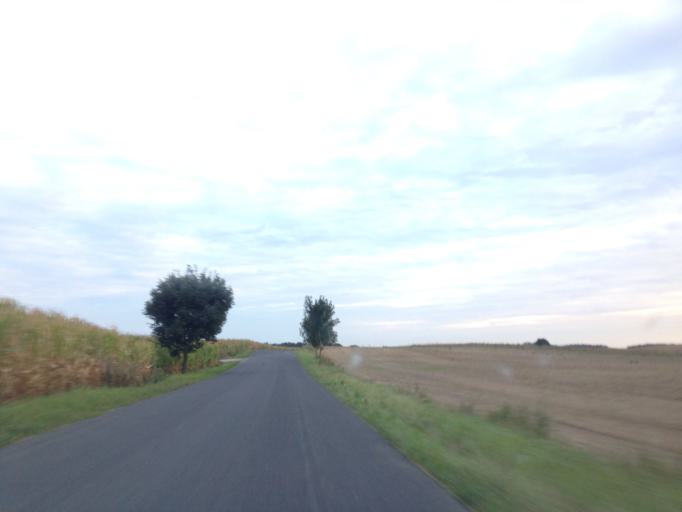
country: PL
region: Kujawsko-Pomorskie
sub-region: Powiat brodnicki
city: Brzozie
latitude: 53.3125
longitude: 19.6784
